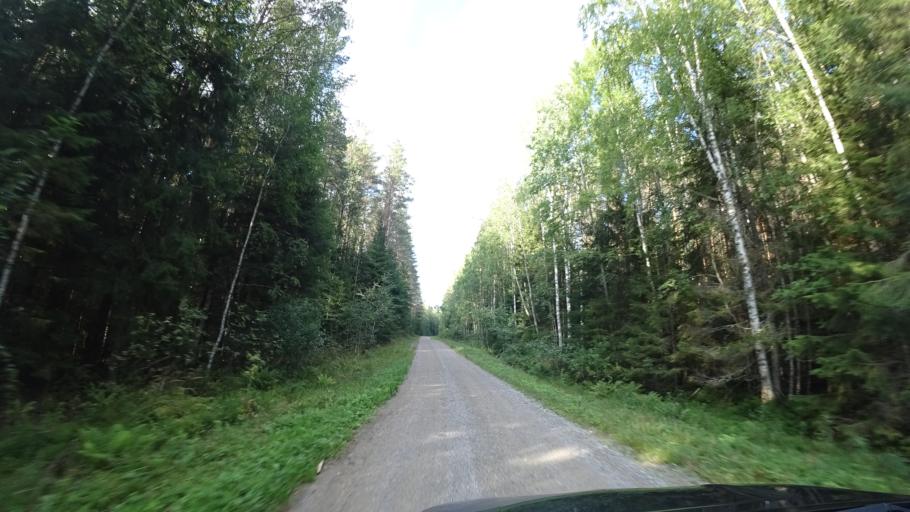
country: FI
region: Paijanne Tavastia
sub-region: Lahti
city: Auttoinen
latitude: 61.2159
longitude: 25.1767
